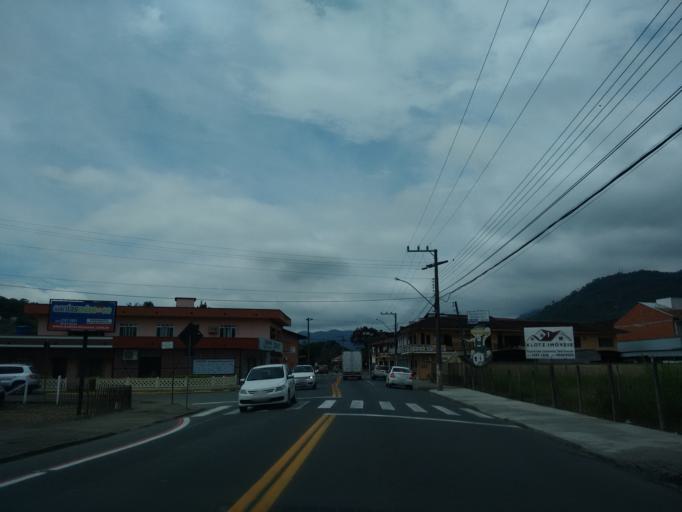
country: BR
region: Santa Catarina
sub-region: Pomerode
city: Pomerode
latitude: -26.7250
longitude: -49.1705
